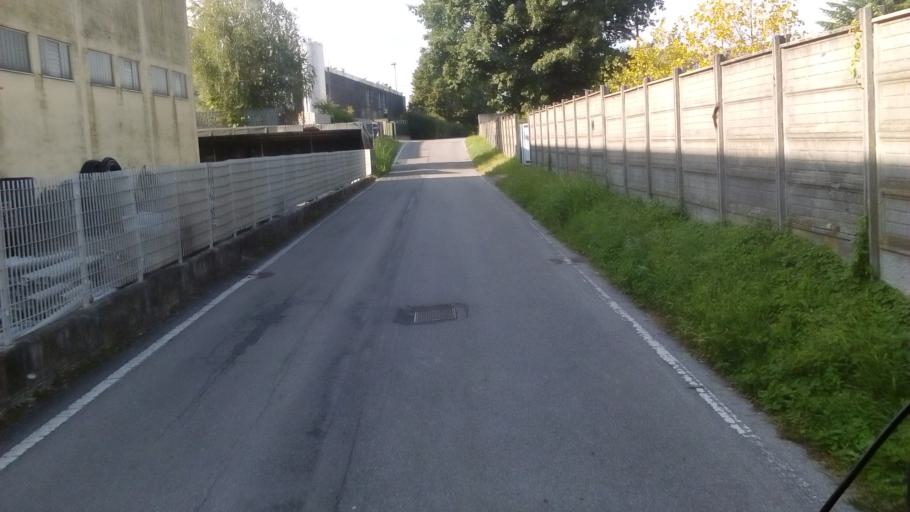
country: IT
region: Lombardy
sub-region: Provincia di Monza e Brianza
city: Albiate
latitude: 45.6535
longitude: 9.2428
